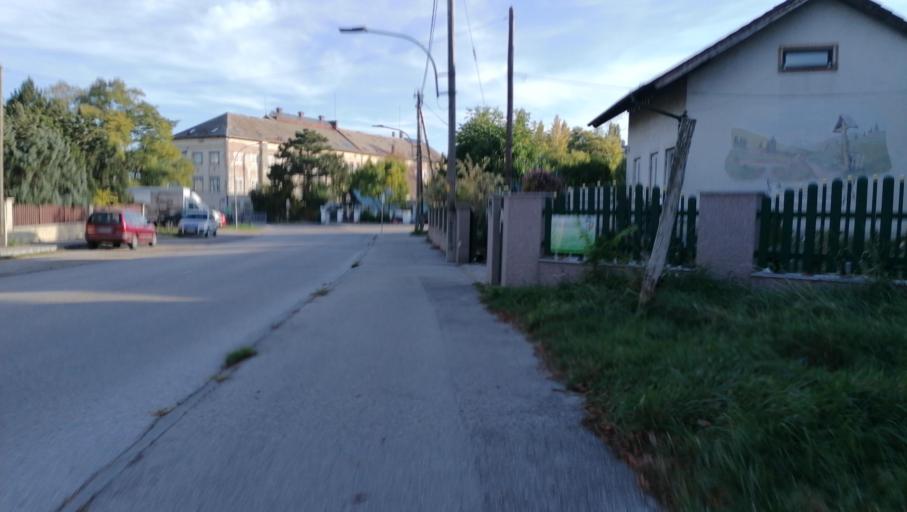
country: AT
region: Lower Austria
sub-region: Politischer Bezirk Baden
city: Pfaffstatten
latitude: 47.9916
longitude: 16.2566
